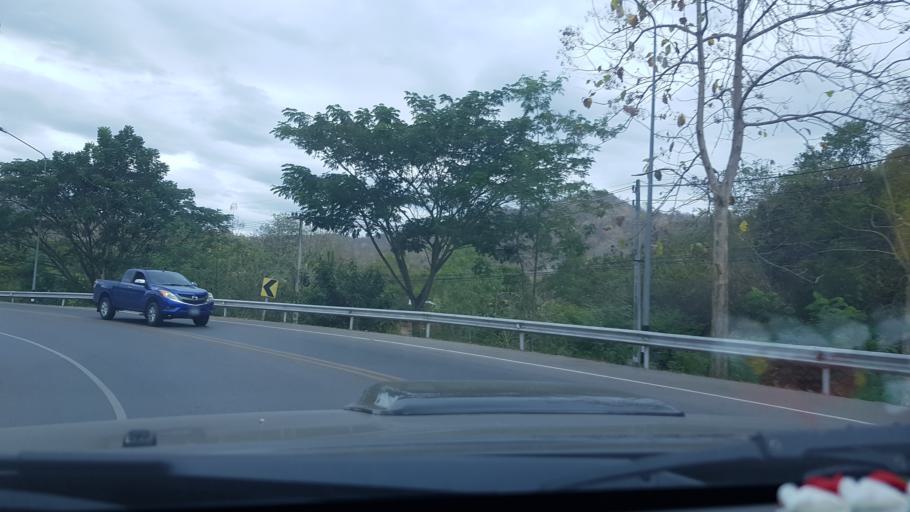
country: TH
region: Phetchabun
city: Phetchabun
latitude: 16.5335
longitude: 101.1013
